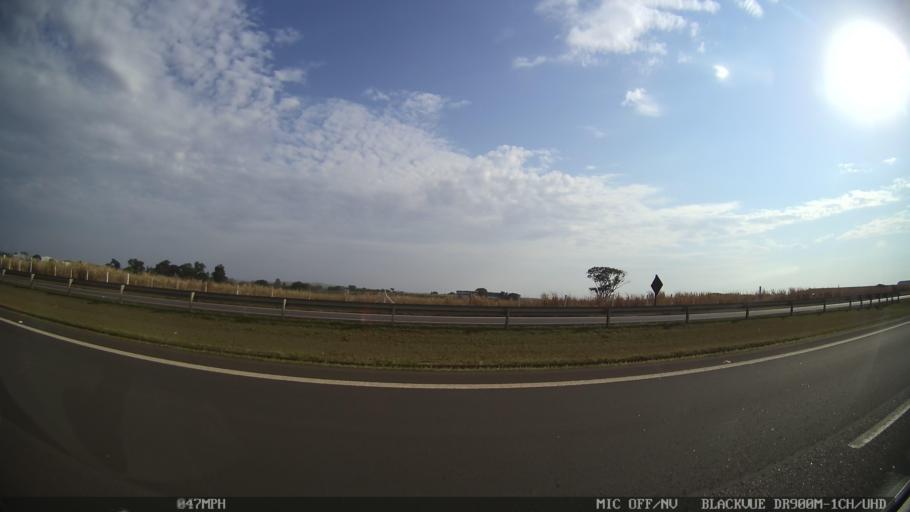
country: BR
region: Sao Paulo
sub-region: Cosmopolis
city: Cosmopolis
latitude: -22.6755
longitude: -47.1600
